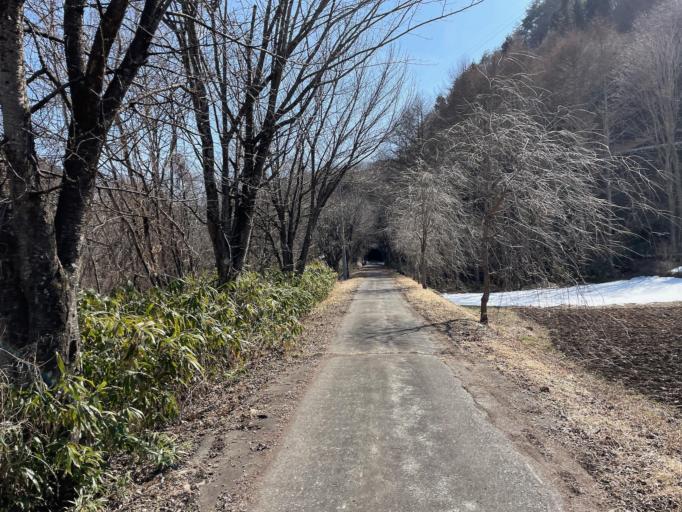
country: JP
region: Gunma
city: Nakanojomachi
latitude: 36.5659
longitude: 138.6356
